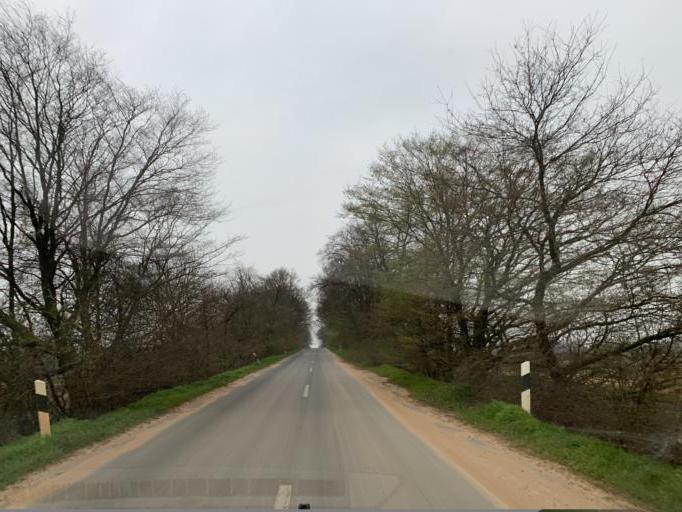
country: DE
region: North Rhine-Westphalia
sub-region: Regierungsbezirk Koln
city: Elsdorf
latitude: 50.8927
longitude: 6.5908
